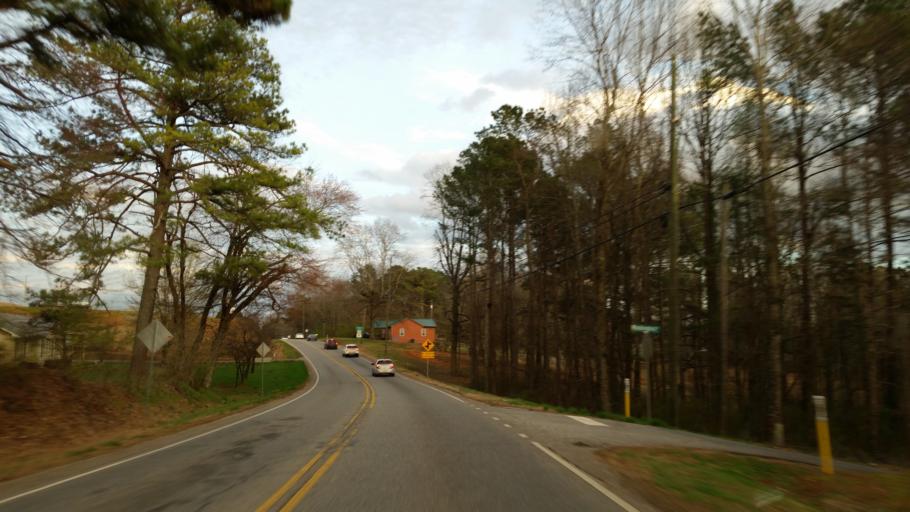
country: US
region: Georgia
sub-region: Pickens County
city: Jasper
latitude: 34.4646
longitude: -84.4769
